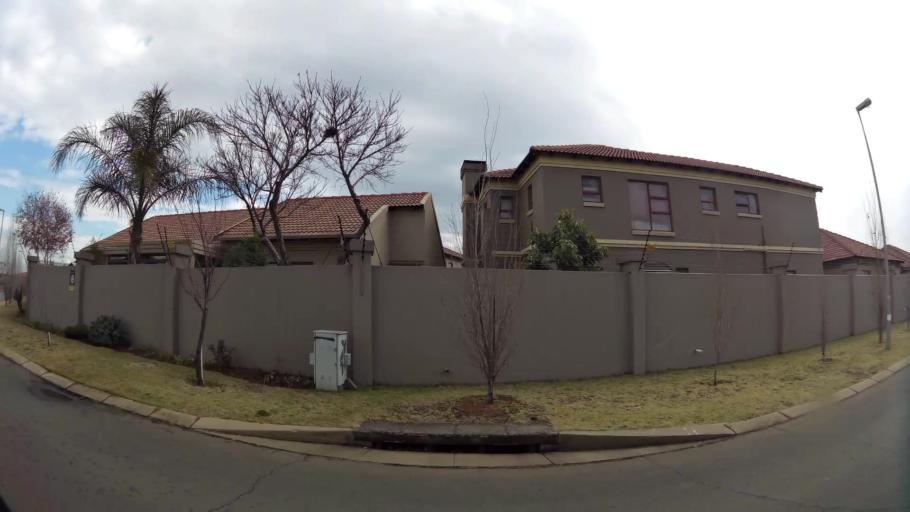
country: ZA
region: Gauteng
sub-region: Sedibeng District Municipality
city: Vanderbijlpark
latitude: -26.7266
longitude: 27.8673
